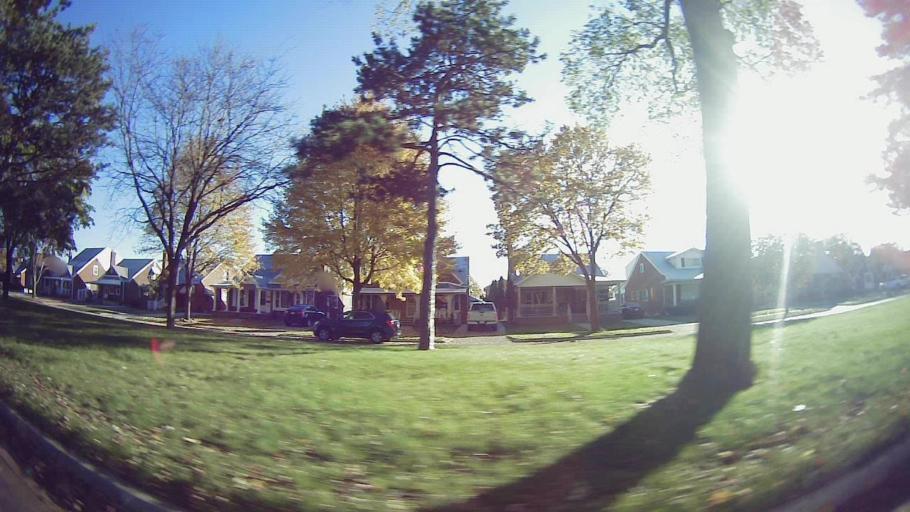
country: US
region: Michigan
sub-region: Wayne County
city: Dearborn
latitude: 42.3355
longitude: -83.1693
